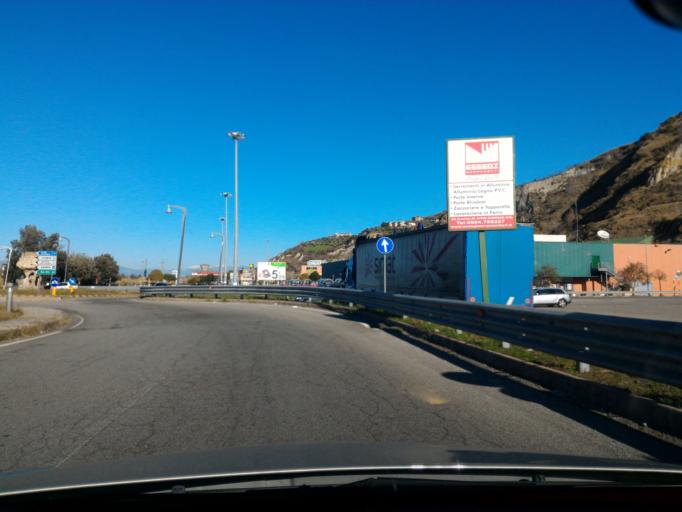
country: IT
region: Calabria
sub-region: Provincia di Cosenza
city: Cosenza
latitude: 39.3108
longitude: 16.2630
